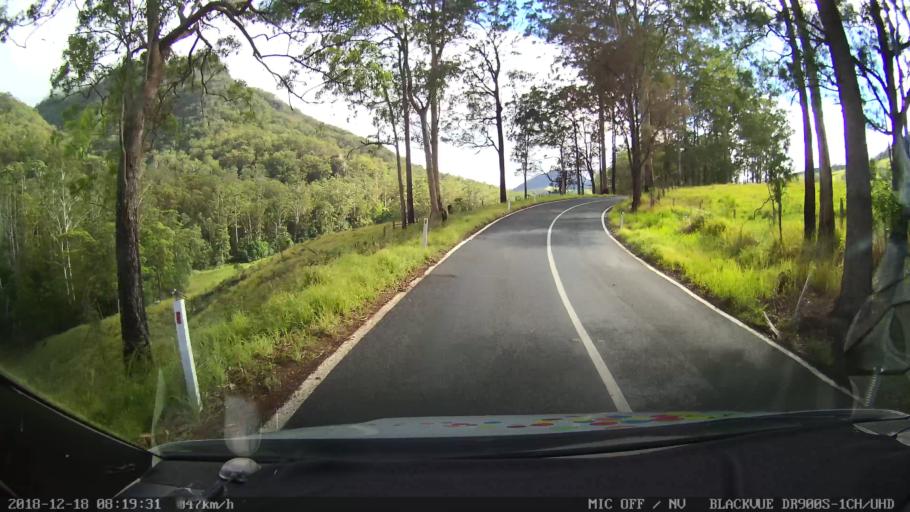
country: AU
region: New South Wales
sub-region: Kyogle
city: Kyogle
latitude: -28.3316
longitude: 152.7094
